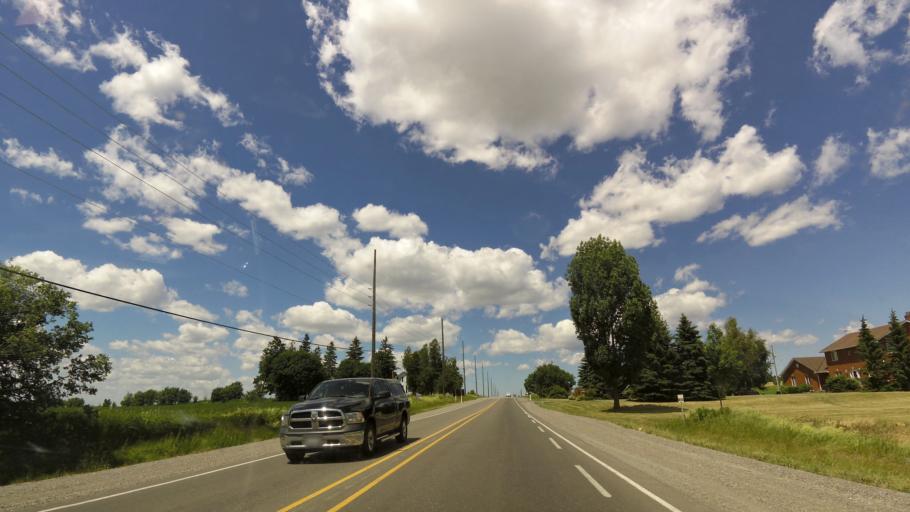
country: CA
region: Ontario
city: Oshawa
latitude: 43.9595
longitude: -78.8583
